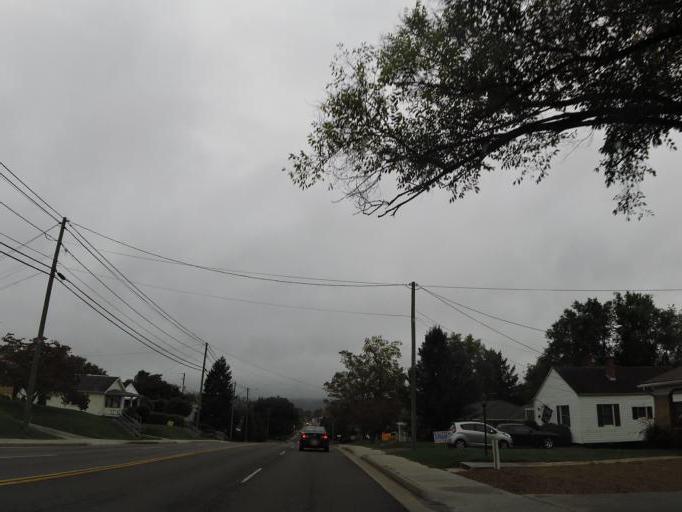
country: US
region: Virginia
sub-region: Wythe County
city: Wytheville
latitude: 36.9535
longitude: -81.0911
